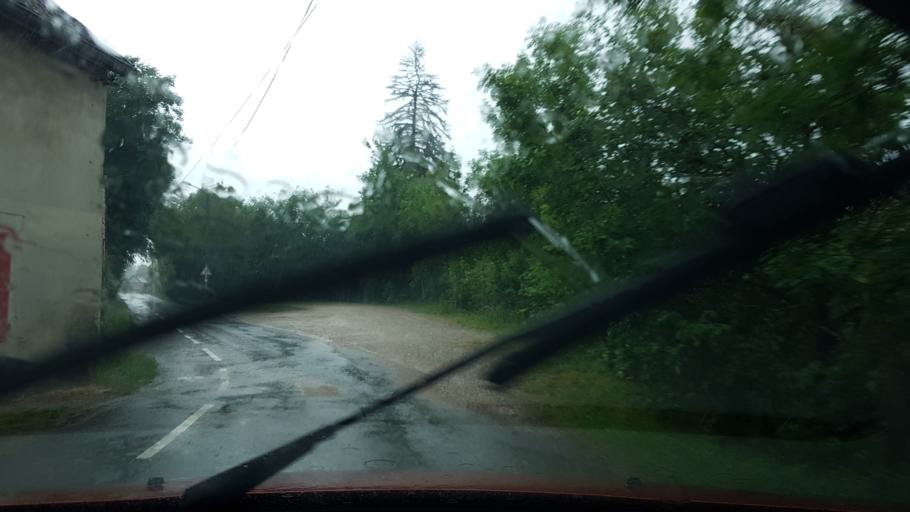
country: FR
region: Franche-Comte
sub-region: Departement du Jura
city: Clairvaux-les-Lacs
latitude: 46.5808
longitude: 5.7021
